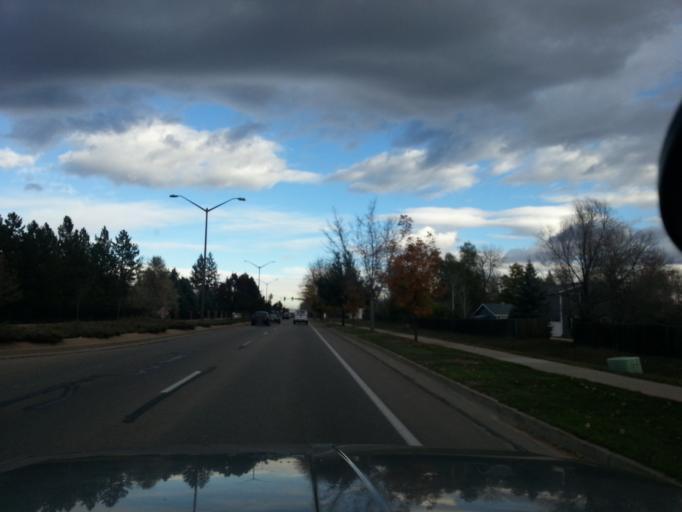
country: US
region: Colorado
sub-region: Larimer County
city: Fort Collins
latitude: 40.5419
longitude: -105.1151
